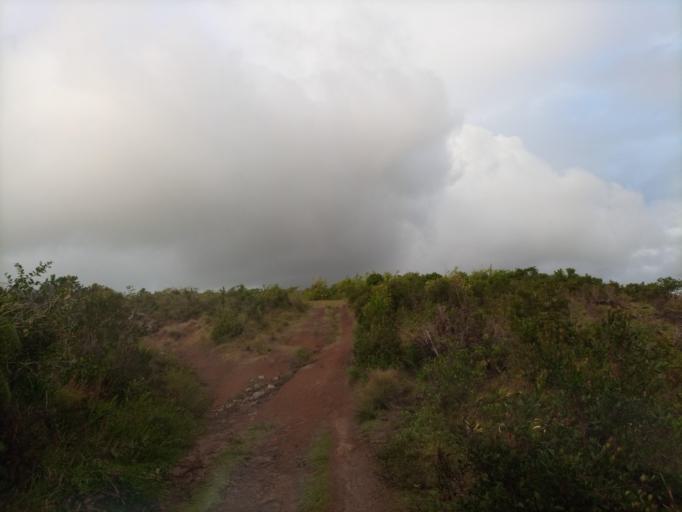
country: MG
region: Anosy
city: Fort Dauphin
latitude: -24.7024
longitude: 47.1781
